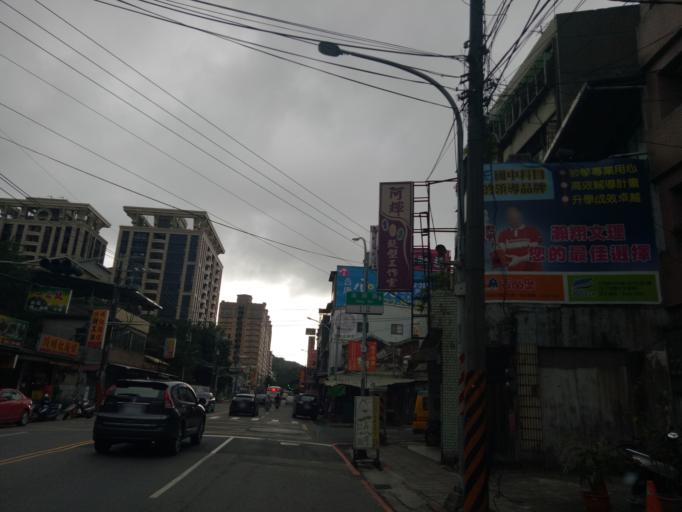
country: TW
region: Taipei
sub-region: Taipei
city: Banqiao
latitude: 24.9561
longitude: 121.4139
